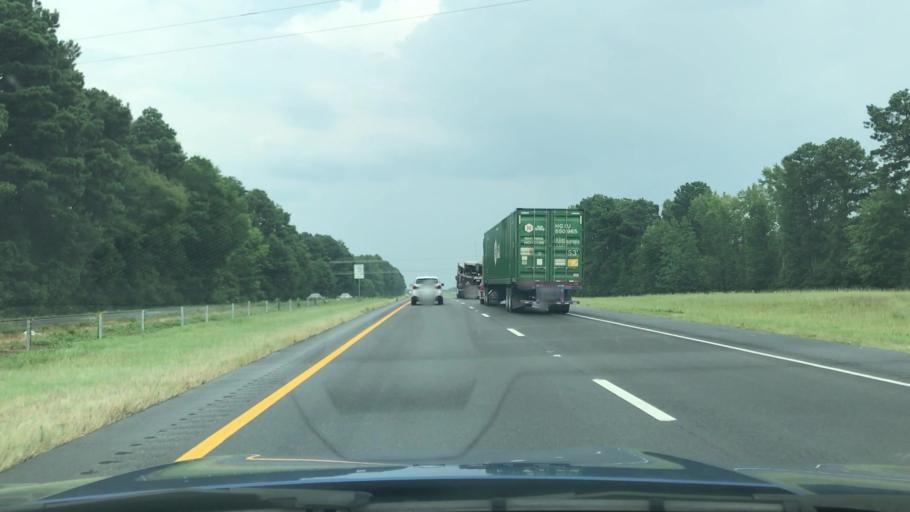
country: US
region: Texas
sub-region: Harrison County
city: Hallsville
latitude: 32.4854
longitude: -94.4941
